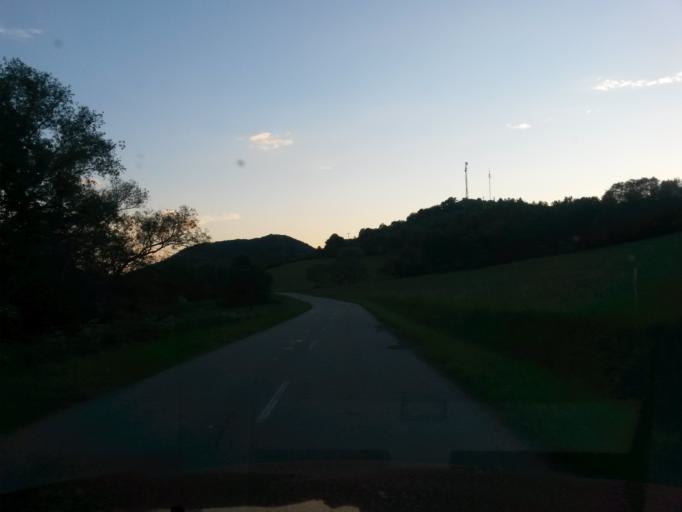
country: UA
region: Zakarpattia
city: Kamianytsia
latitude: 48.8058
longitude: 22.3147
